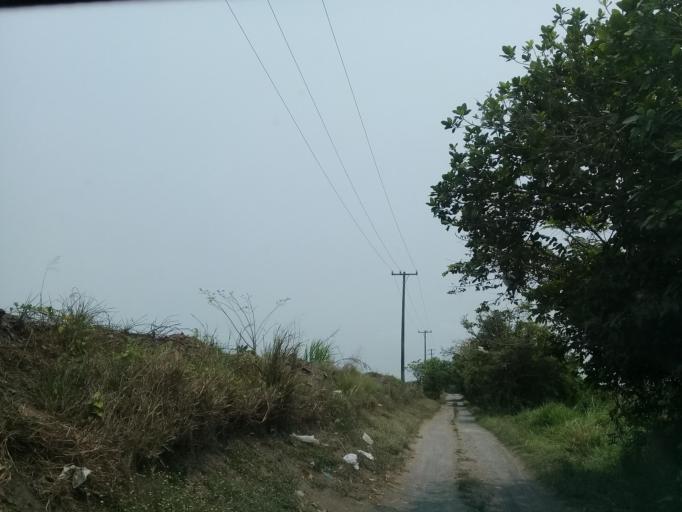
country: MX
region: Veracruz
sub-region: Veracruz
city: Hacienda Sotavento
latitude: 19.1434
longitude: -96.1593
